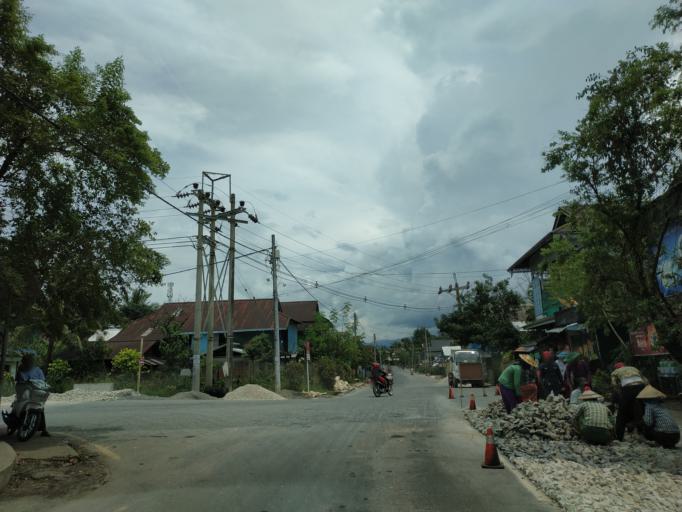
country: MM
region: Tanintharyi
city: Dawei
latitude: 14.0725
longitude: 98.2075
